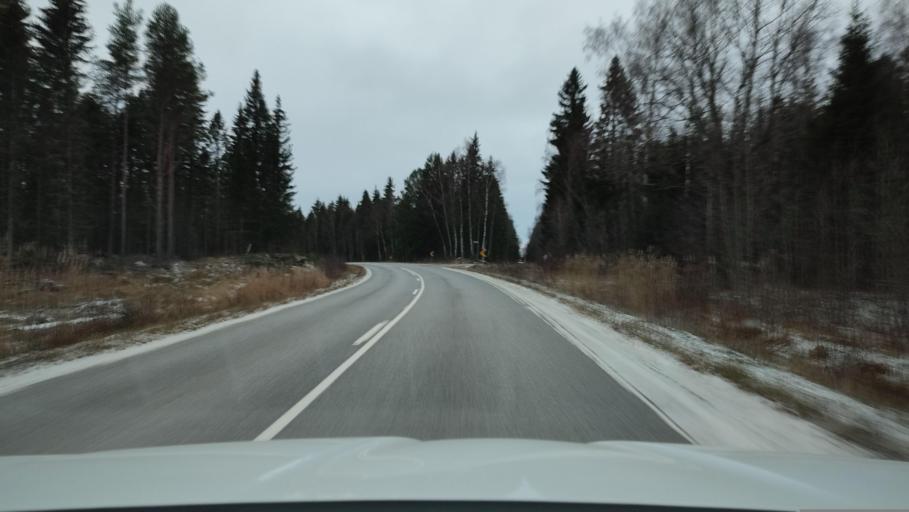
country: FI
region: Ostrobothnia
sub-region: Vaasa
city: Replot
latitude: 63.2642
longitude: 21.3585
